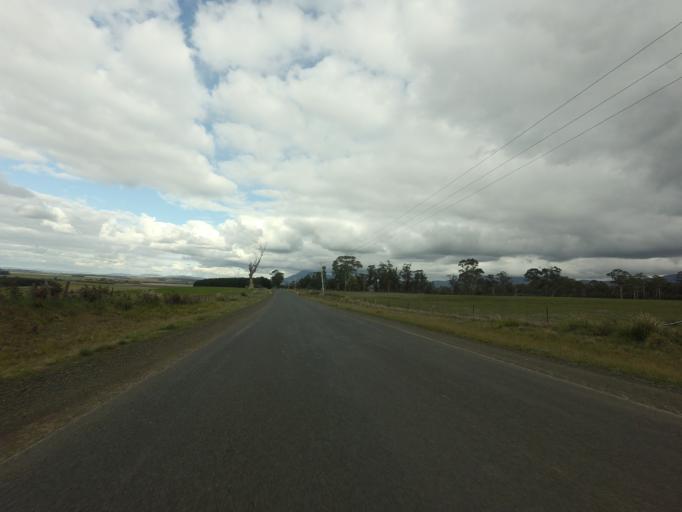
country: AU
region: Tasmania
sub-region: Northern Midlands
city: Longford
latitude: -41.7644
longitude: 147.0839
